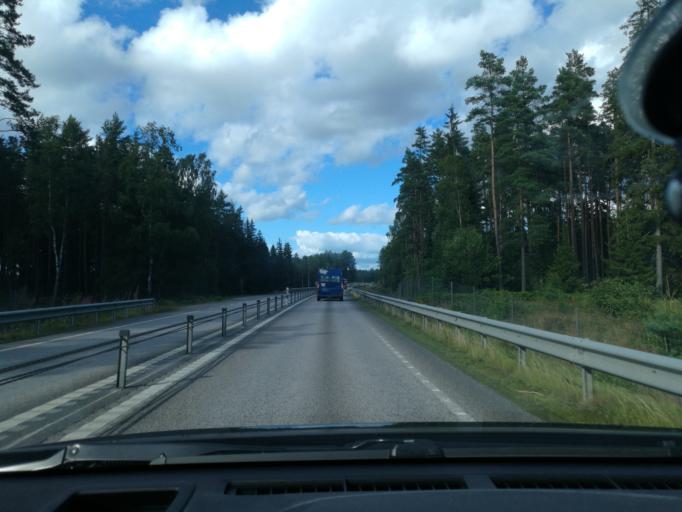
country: SE
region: Kronoberg
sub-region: Vaxjo Kommun
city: Braas
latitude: 57.0288
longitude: 15.0627
